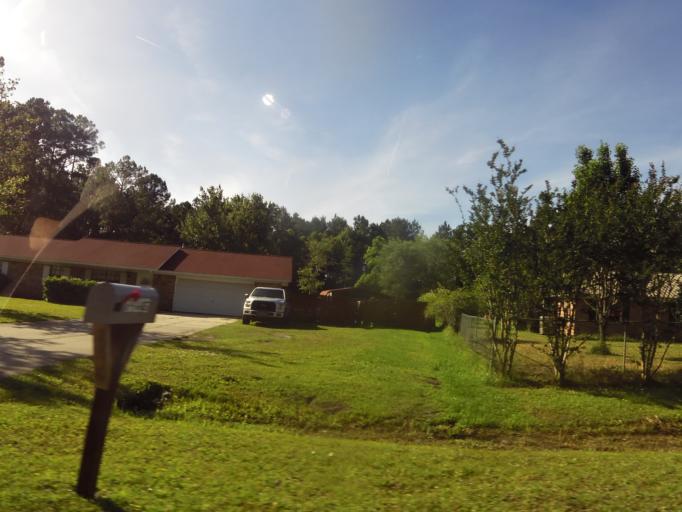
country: US
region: Florida
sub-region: Nassau County
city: Nassau Village-Ratliff
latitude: 30.5258
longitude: -81.7762
